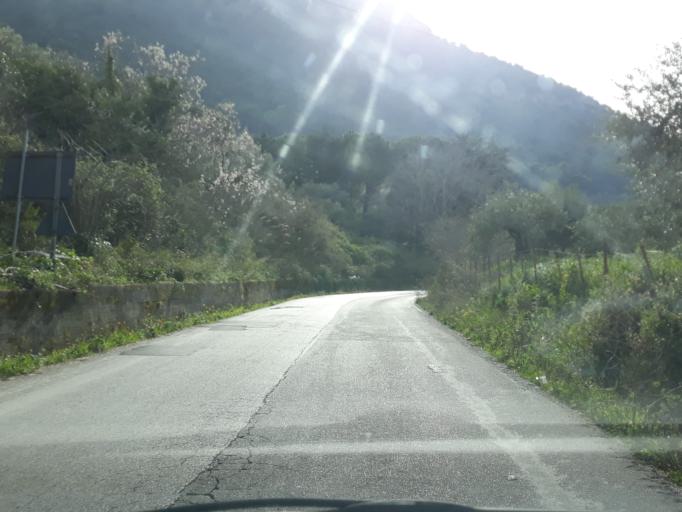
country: IT
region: Sicily
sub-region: Palermo
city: Piano Maglio-Blandino
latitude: 38.0403
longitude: 13.3144
